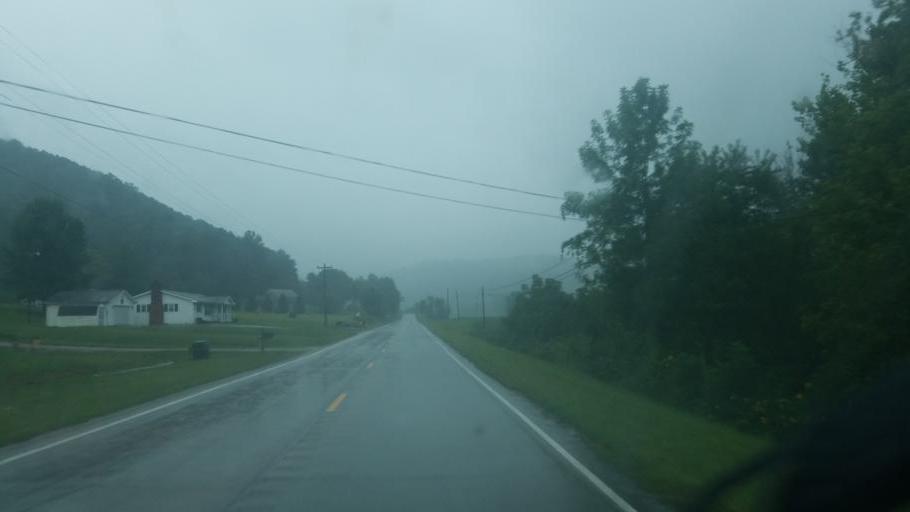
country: US
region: Kentucky
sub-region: Rowan County
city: Morehead
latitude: 38.2929
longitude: -83.5705
